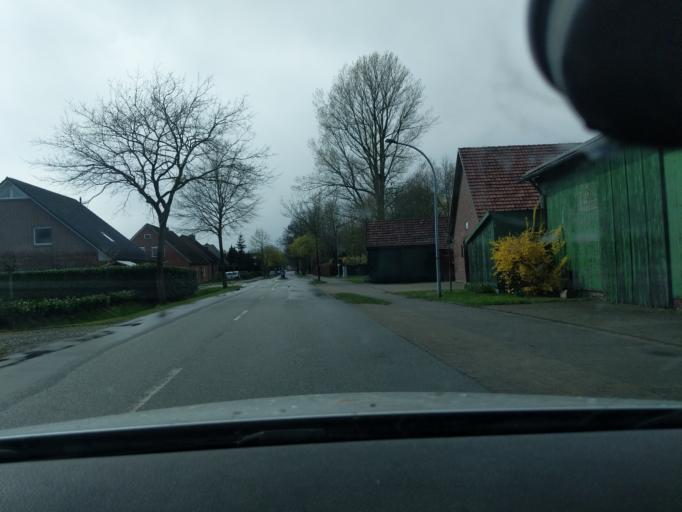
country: DE
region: Lower Saxony
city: Ahlerstedt
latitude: 53.4017
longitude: 9.4594
